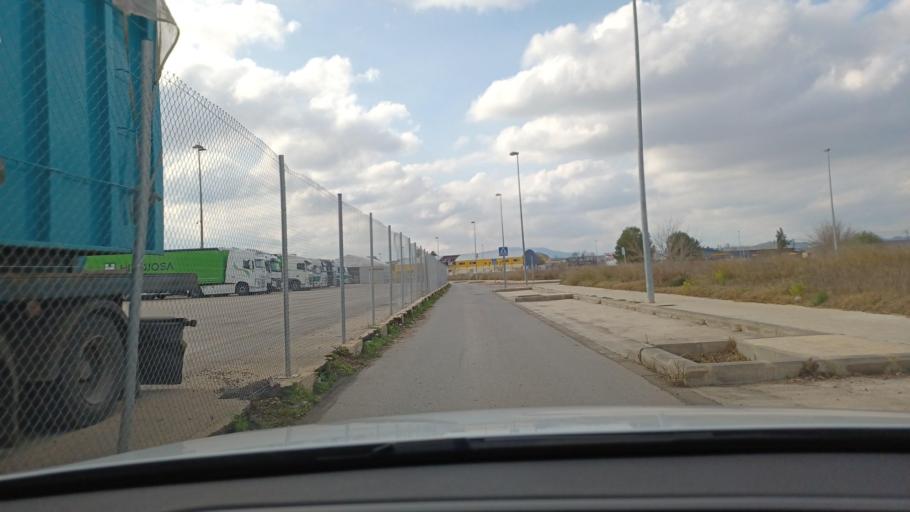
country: ES
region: Valencia
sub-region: Provincia de Valencia
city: Xativa
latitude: 38.9964
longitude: -0.5088
